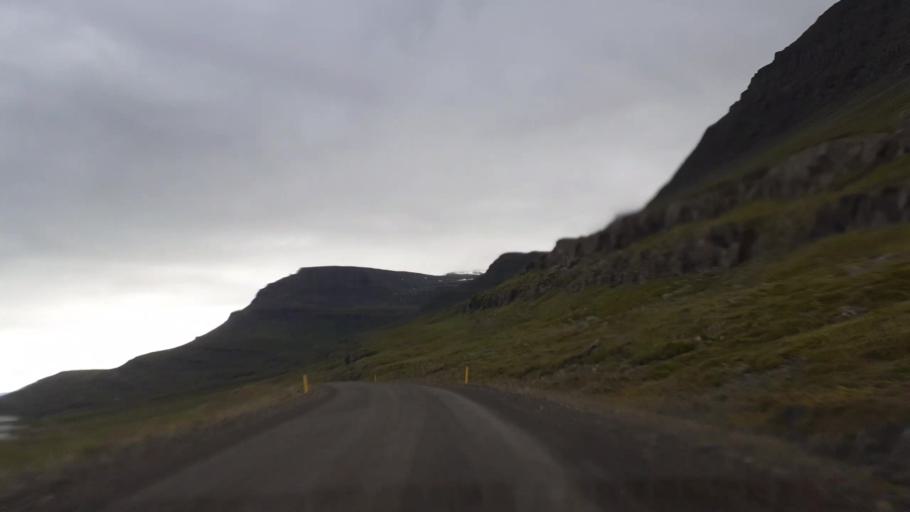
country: IS
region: East
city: Reydarfjoerdur
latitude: 65.0132
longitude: -14.1855
